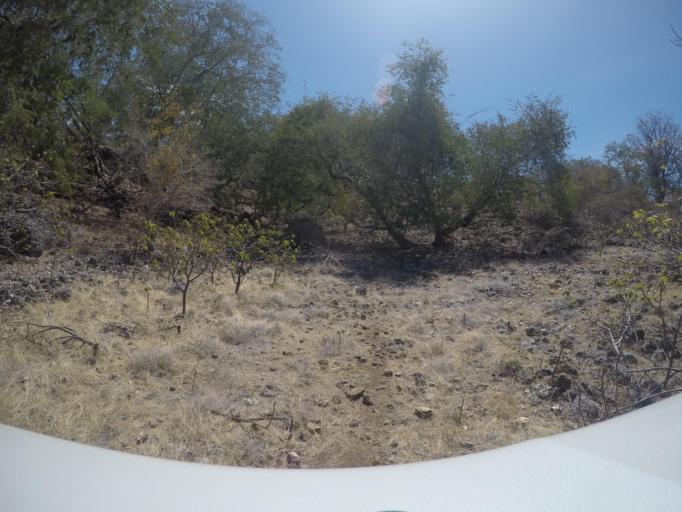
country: TL
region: Baucau
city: Baucau
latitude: -8.4307
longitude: 126.4422
